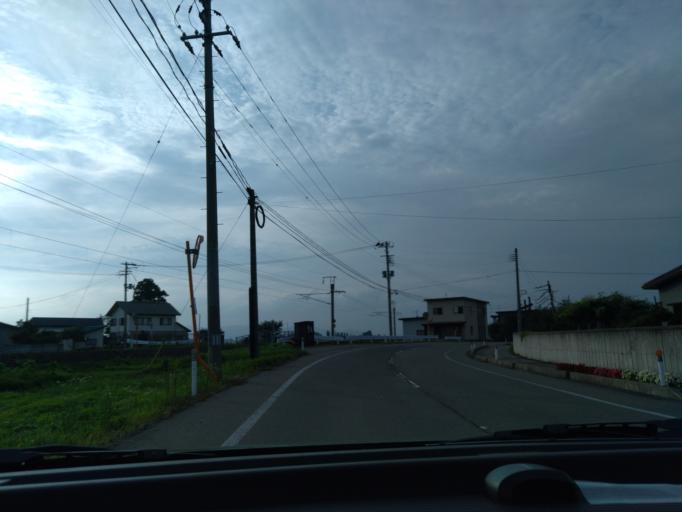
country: JP
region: Akita
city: Omagari
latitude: 39.3883
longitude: 140.5257
